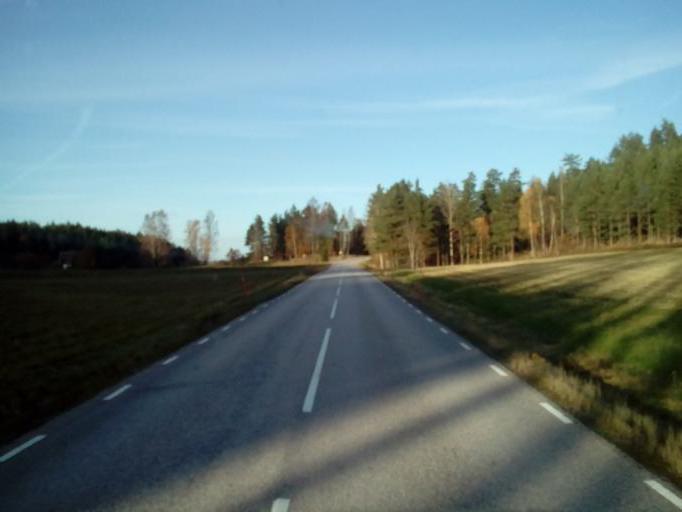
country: SE
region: Kalmar
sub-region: Vasterviks Kommun
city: Ankarsrum
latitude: 57.7802
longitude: 16.1646
